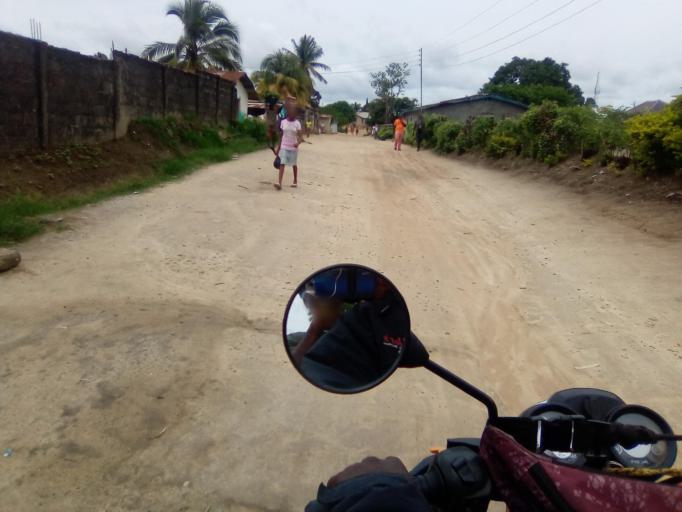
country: SL
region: Southern Province
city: Bo
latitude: 7.9431
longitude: -11.7309
